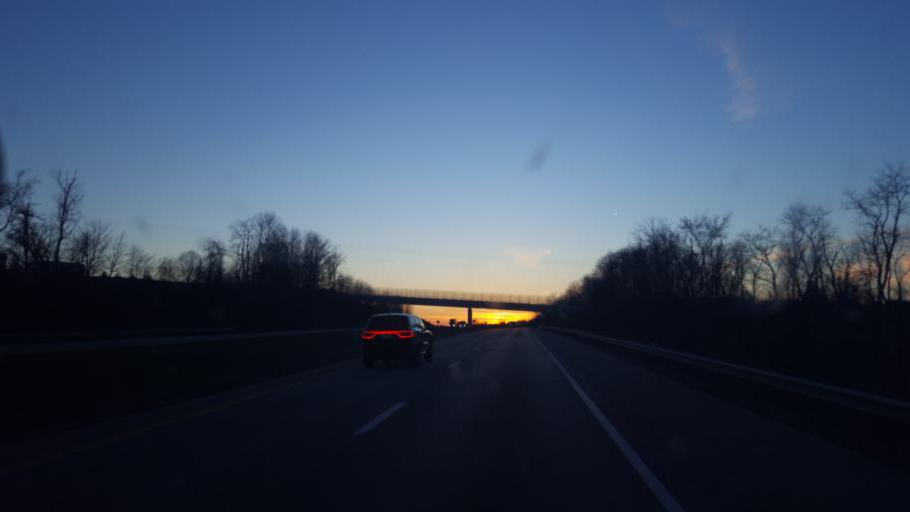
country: US
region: Ohio
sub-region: Belmont County
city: Bethesda
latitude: 40.0650
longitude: -81.0292
